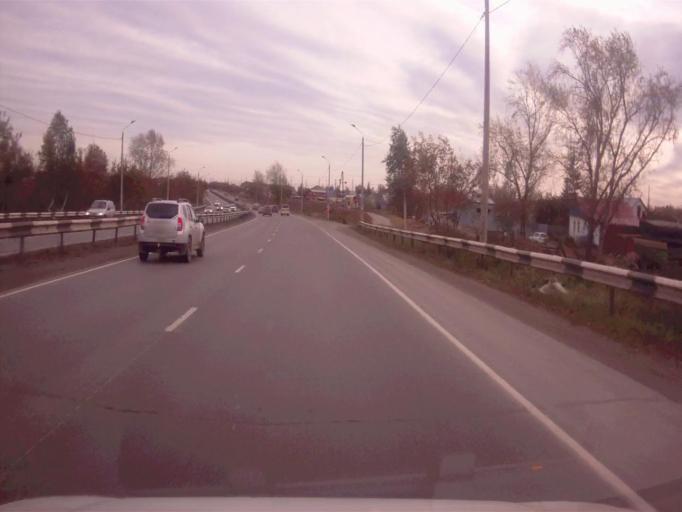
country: RU
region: Chelyabinsk
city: Novosineglazovskiy
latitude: 55.0477
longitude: 61.4160
